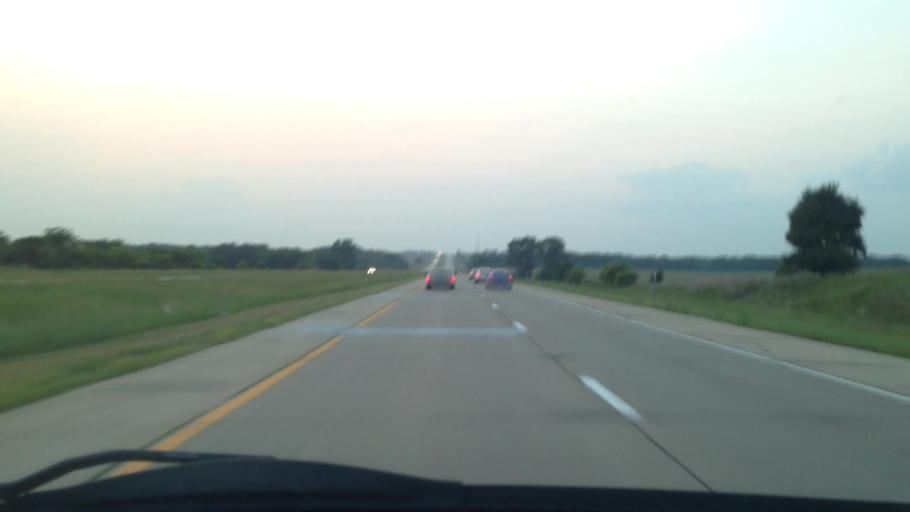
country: US
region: Iowa
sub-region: Benton County
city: Urbana
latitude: 42.2917
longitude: -91.9526
